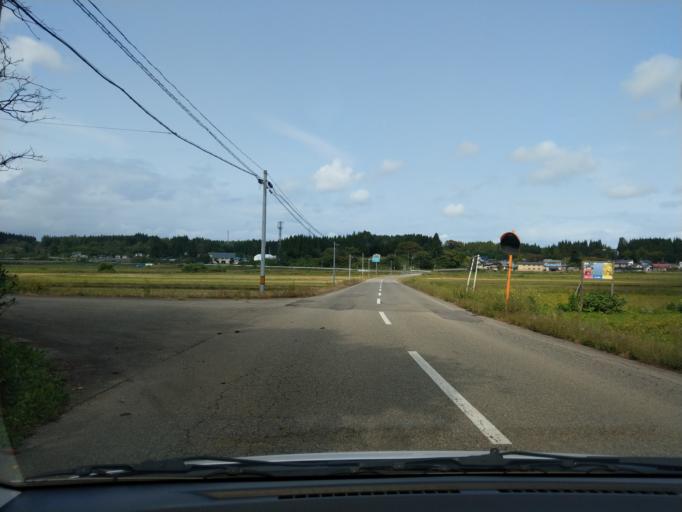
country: JP
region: Akita
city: Omagari
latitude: 39.5165
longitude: 140.3061
